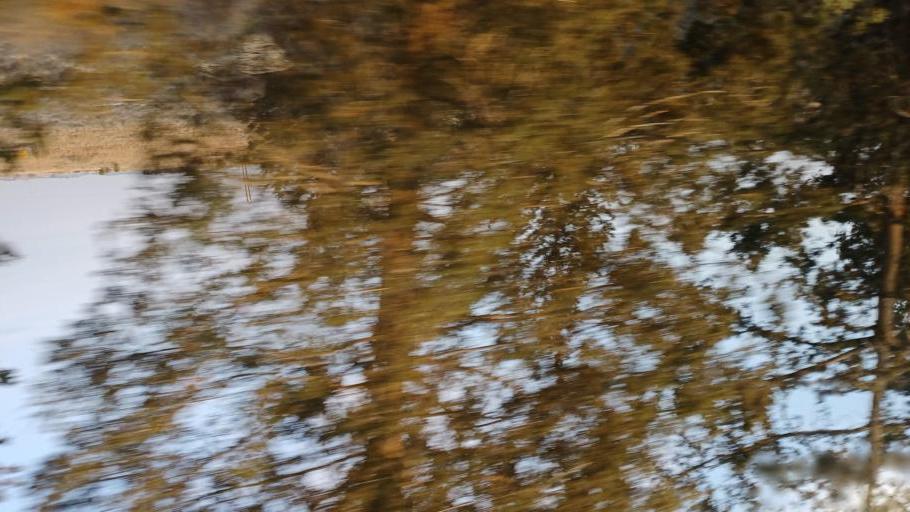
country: CY
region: Lefkosia
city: Lympia
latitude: 35.0100
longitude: 33.4969
